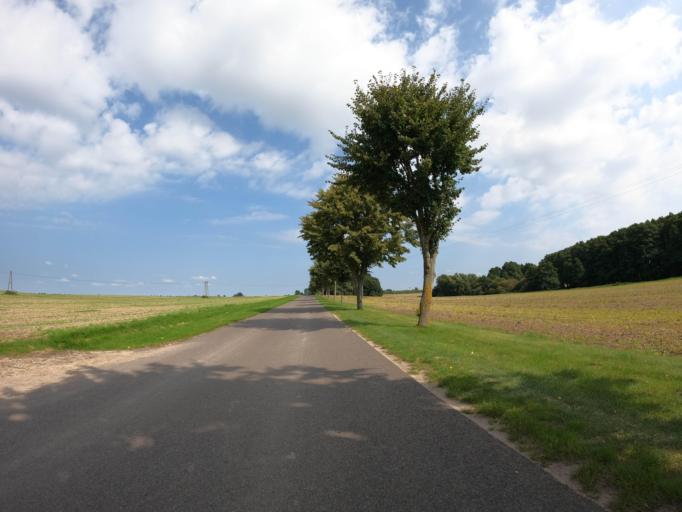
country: DE
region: Mecklenburg-Vorpommern
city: Malchow
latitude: 53.4537
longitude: 12.4713
